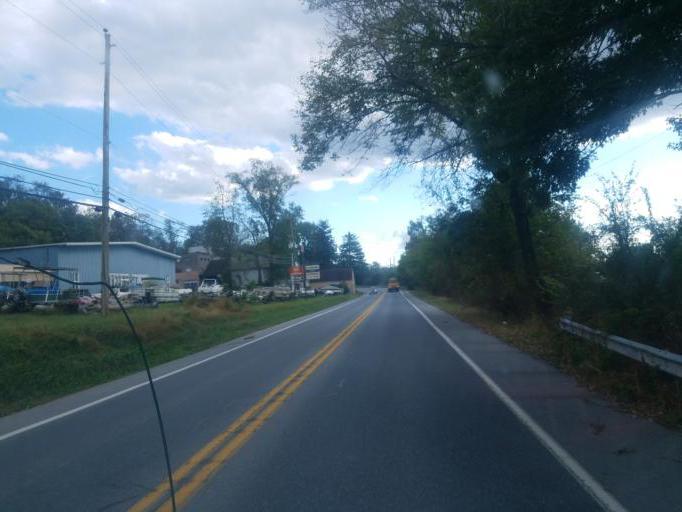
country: US
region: Pennsylvania
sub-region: Dauphin County
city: Middletown
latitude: 40.1729
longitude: -76.7236
